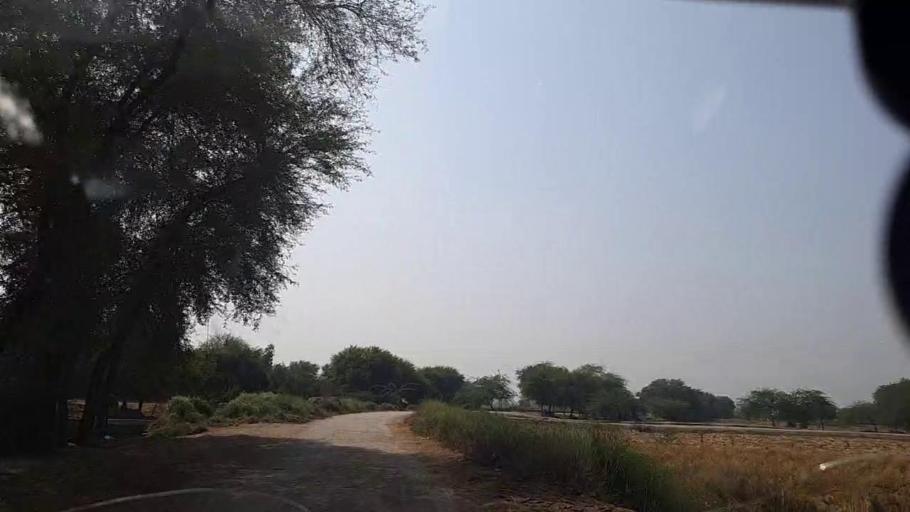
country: PK
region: Sindh
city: Shikarpur
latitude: 27.9864
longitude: 68.6310
